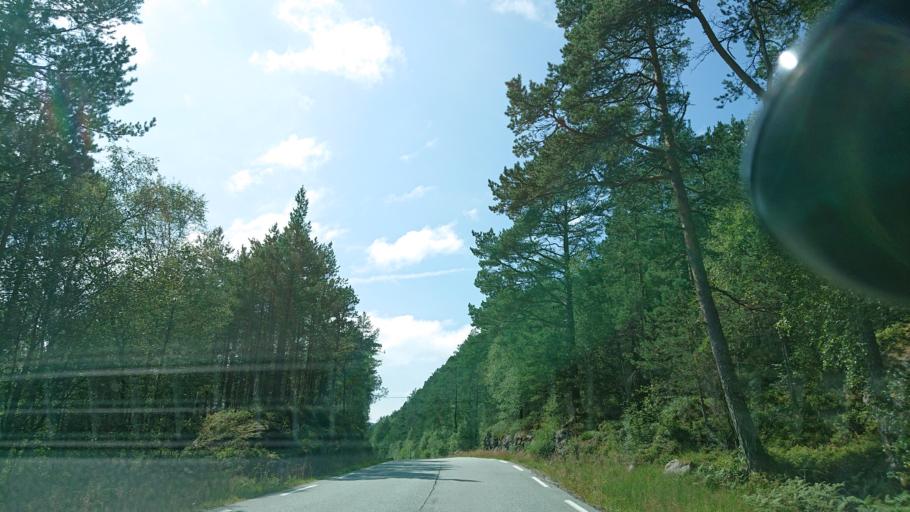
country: NO
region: Rogaland
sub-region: Hjelmeland
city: Hjelmelandsvagen
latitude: 59.2347
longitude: 6.2463
